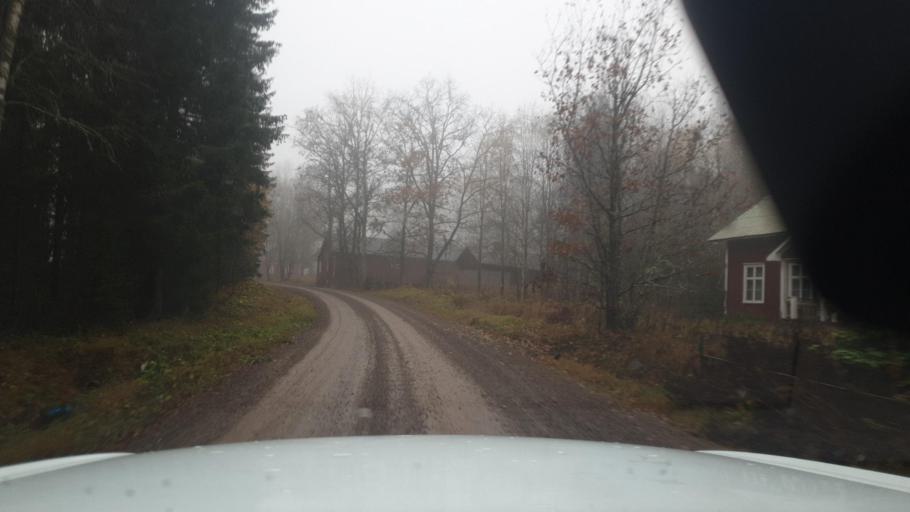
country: SE
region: Vaermland
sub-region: Arvika Kommun
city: Arvika
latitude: 59.9755
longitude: 12.6598
